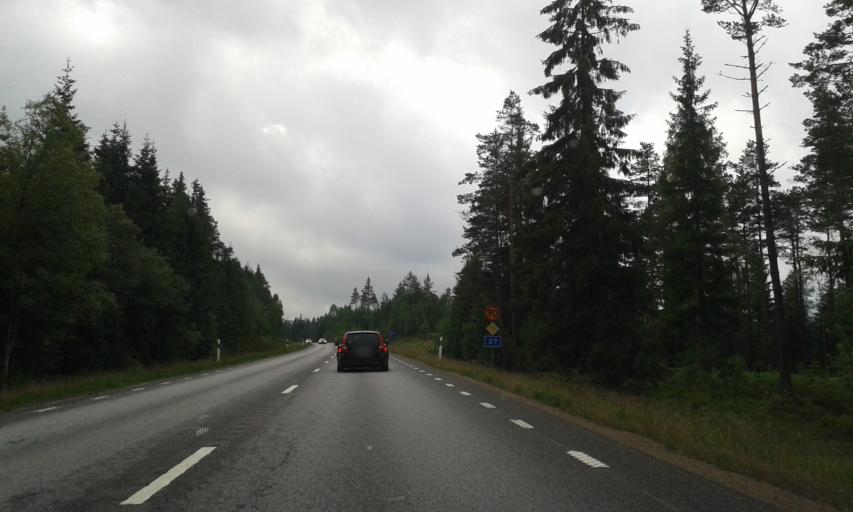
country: SE
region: Joenkoeping
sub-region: Gislaveds Kommun
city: Gislaved
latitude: 57.3814
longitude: 13.4725
